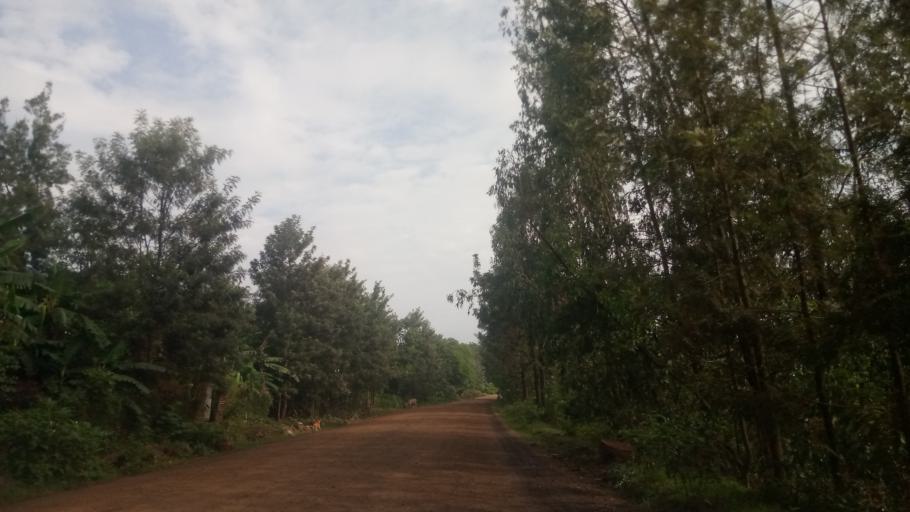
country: ET
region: Oromiya
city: Agaro
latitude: 7.8437
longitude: 36.6592
